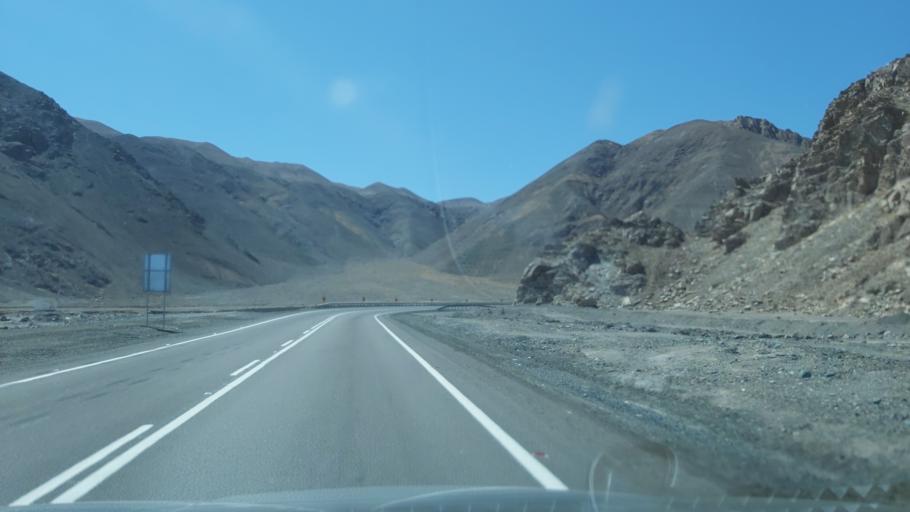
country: CL
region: Atacama
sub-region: Provincia de Chanaral
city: Diego de Almagro
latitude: -26.3379
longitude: -69.7486
